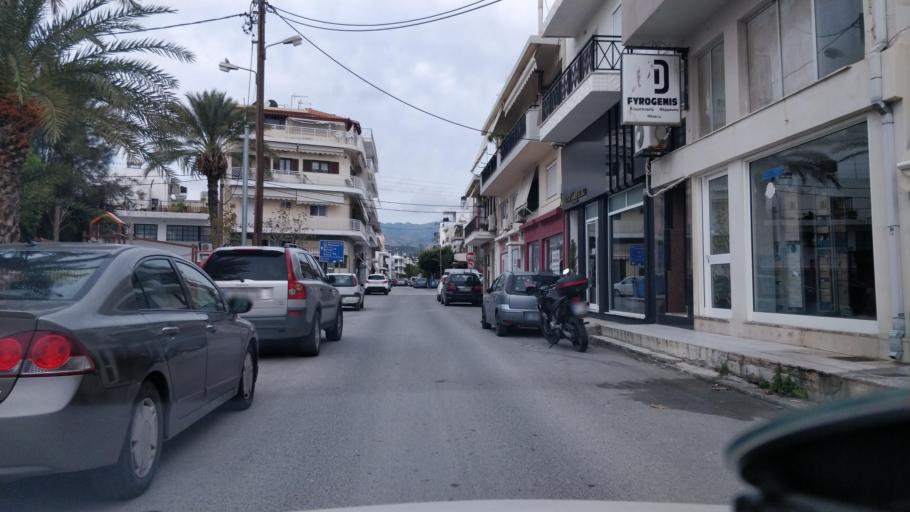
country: GR
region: Crete
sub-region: Nomos Lasithiou
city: Ierapetra
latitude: 35.0068
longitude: 25.7352
